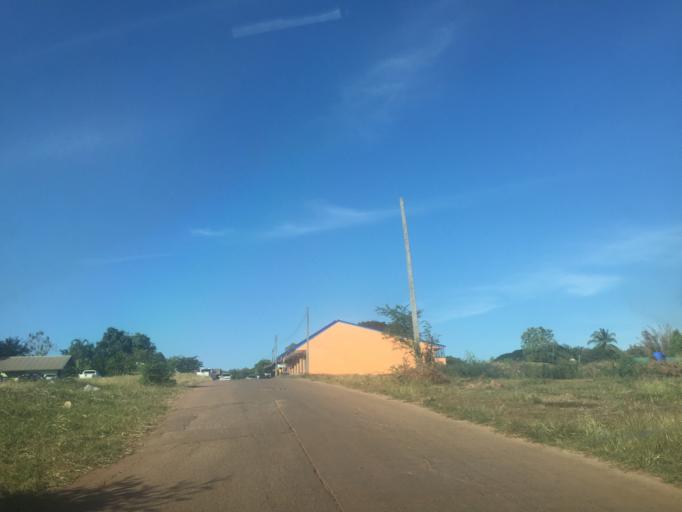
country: TH
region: Changwat Udon Thani
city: Si That
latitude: 16.9715
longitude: 103.2218
